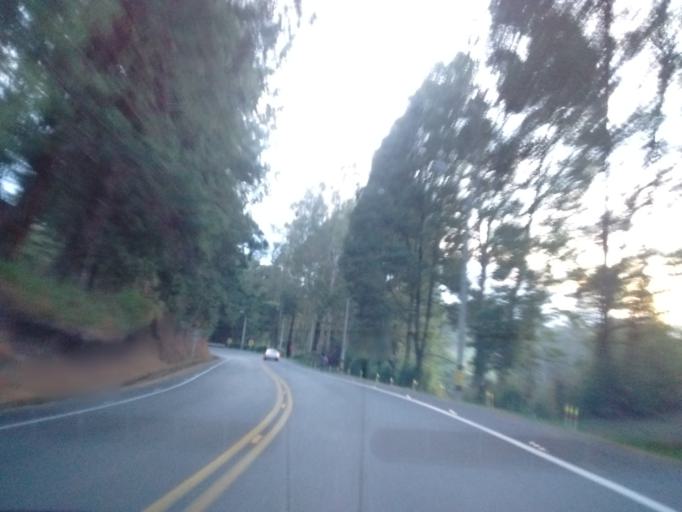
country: CO
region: Antioquia
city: Envigado
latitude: 6.1593
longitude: -75.5318
